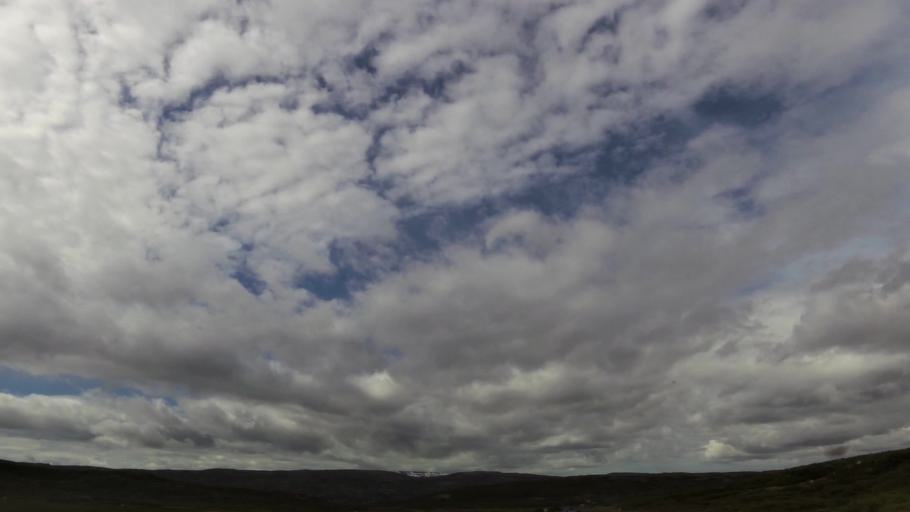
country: IS
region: West
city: Stykkisholmur
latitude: 65.5467
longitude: -22.0974
